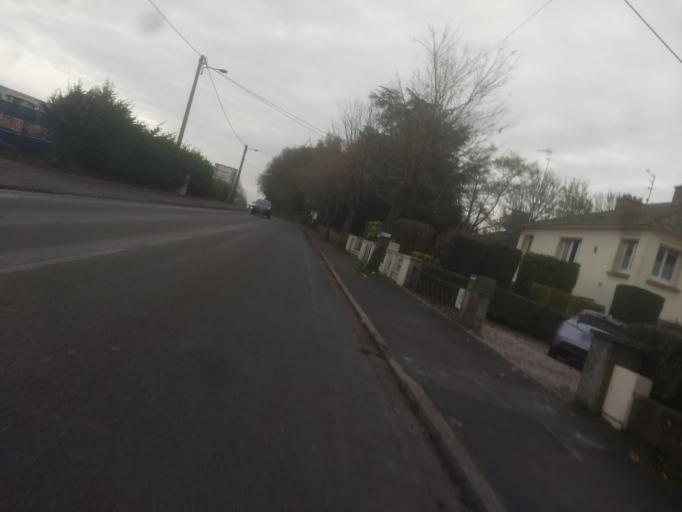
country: FR
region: Nord-Pas-de-Calais
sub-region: Departement du Pas-de-Calais
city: Dainville
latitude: 50.2796
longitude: 2.7345
